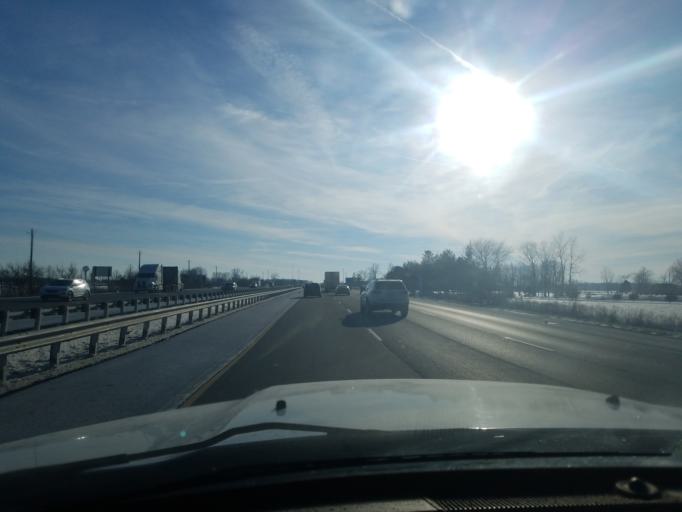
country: US
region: Indiana
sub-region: Madison County
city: Pendleton
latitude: 40.0144
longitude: -85.7669
